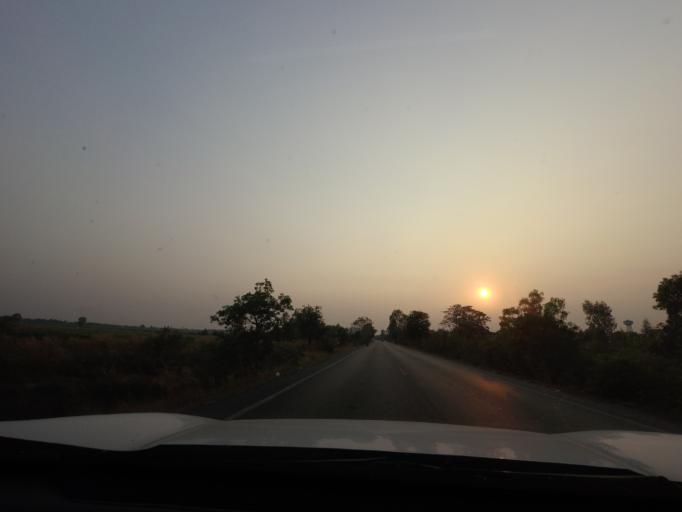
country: TH
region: Nakhon Nayok
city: Ongkharak
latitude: 14.1495
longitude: 101.0358
